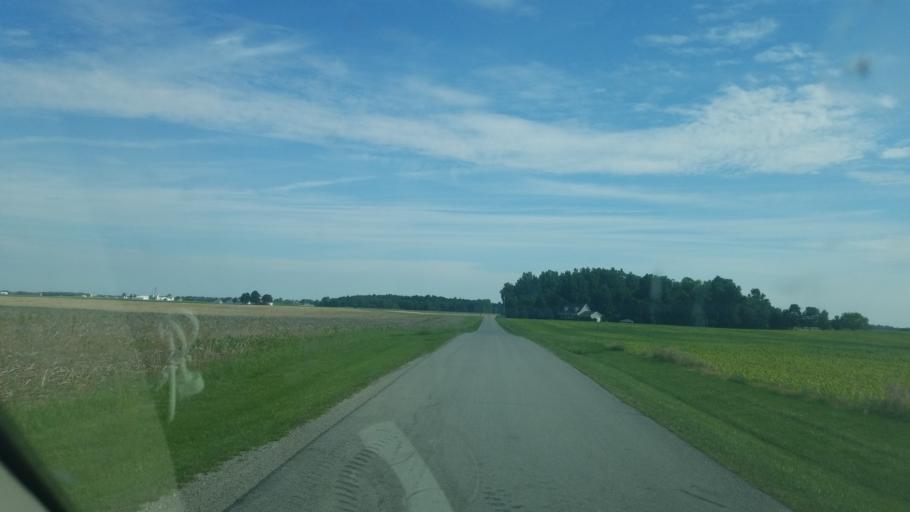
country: US
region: Ohio
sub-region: Wyandot County
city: Upper Sandusky
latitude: 40.7977
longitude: -83.2076
